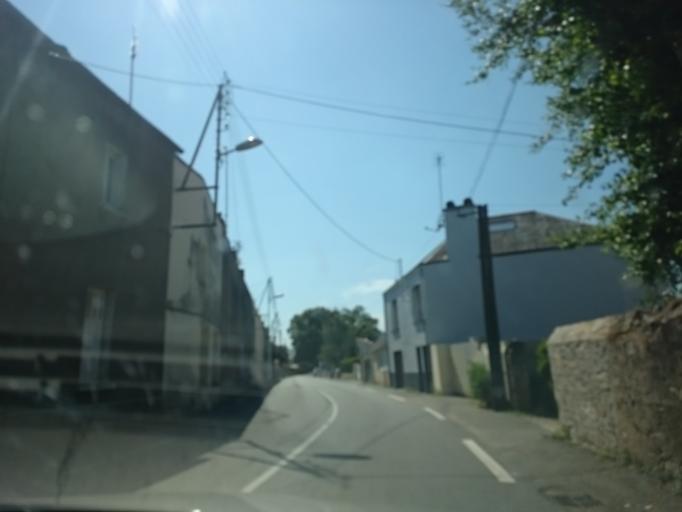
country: FR
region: Pays de la Loire
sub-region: Departement de la Loire-Atlantique
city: Coueron
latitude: 47.2113
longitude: -1.7319
